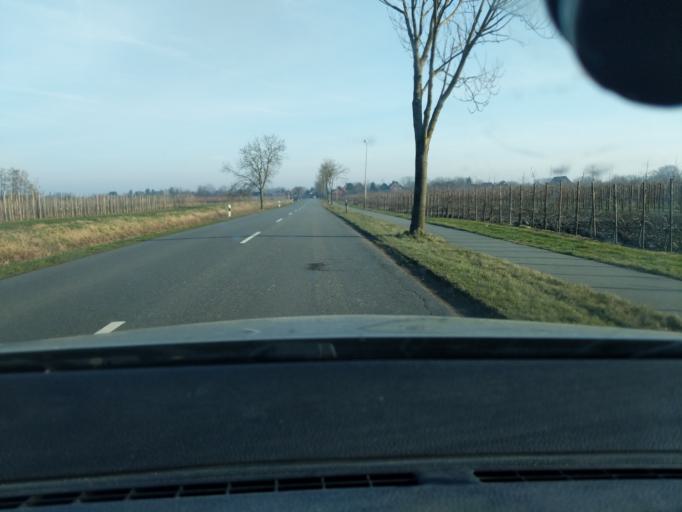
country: DE
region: Lower Saxony
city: Jork
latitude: 53.5461
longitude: 9.6615
